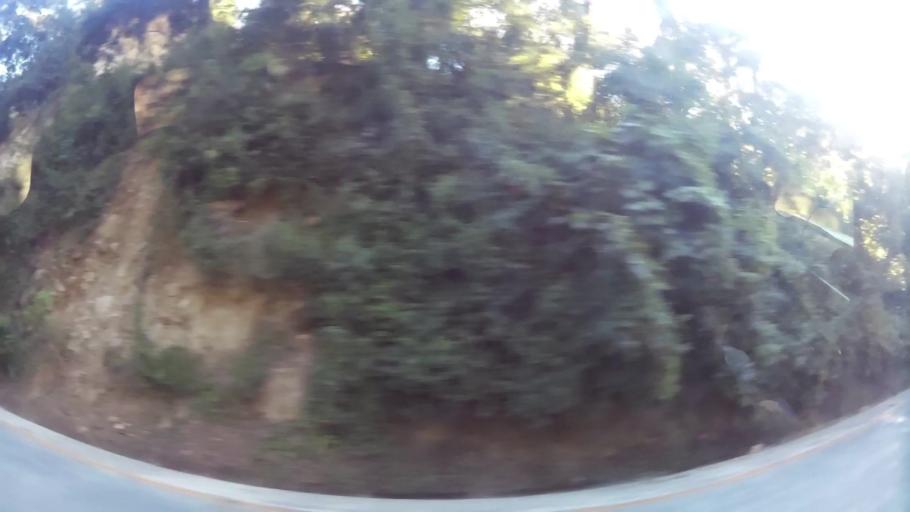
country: GT
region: Sacatepequez
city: Santa Lucia Milpas Altas
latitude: 14.5660
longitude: -90.6960
